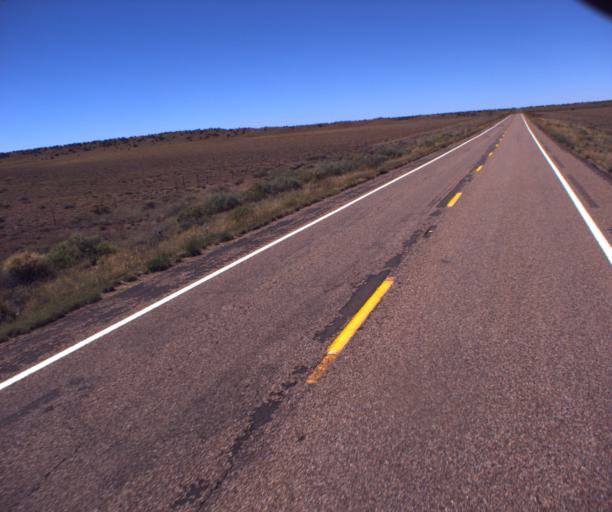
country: US
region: Arizona
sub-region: Apache County
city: Saint Johns
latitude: 34.5886
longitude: -109.5927
